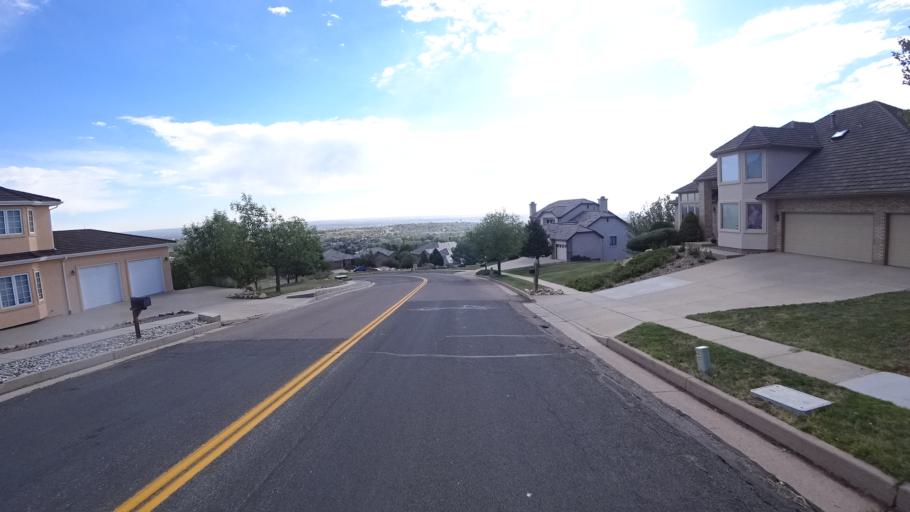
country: US
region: Colorado
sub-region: El Paso County
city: Stratmoor
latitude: 38.7706
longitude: -104.8250
